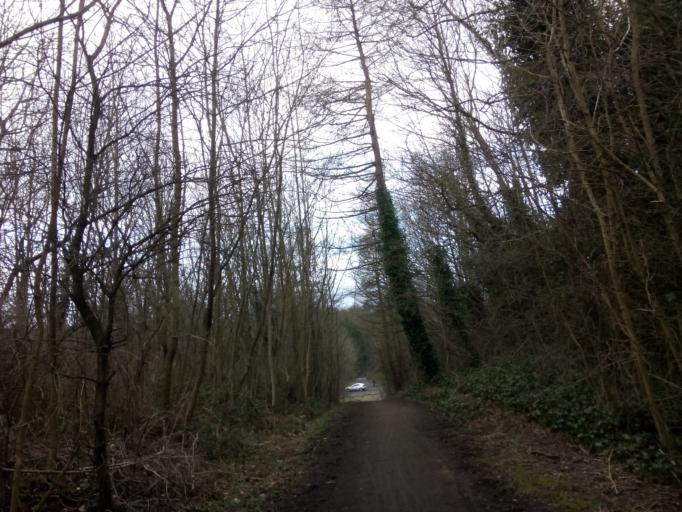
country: GB
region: England
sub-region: County Durham
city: Ushaw Moor
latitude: 54.7740
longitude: -1.6485
